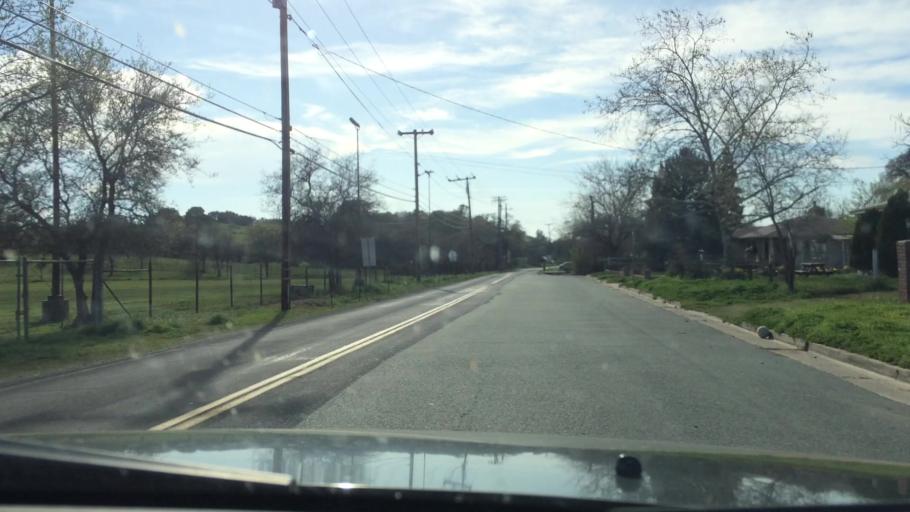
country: US
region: California
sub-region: Amador County
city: Plymouth
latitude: 38.4804
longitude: -120.8533
